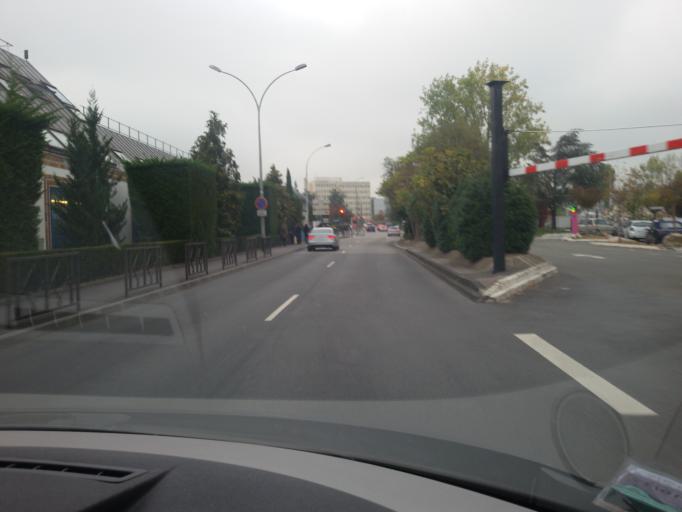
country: FR
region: Ile-de-France
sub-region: Departement de l'Essonne
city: Bievres
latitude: 48.7829
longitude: 2.2195
